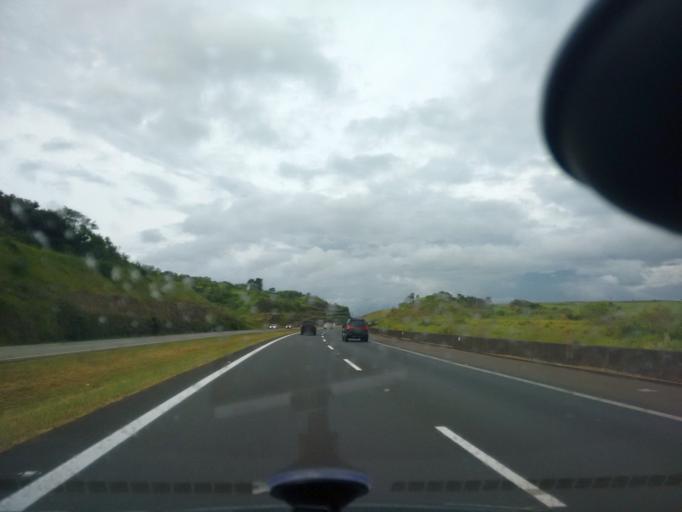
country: BR
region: Sao Paulo
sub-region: Cordeiropolis
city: Cordeiropolis
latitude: -22.5413
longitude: -47.4586
